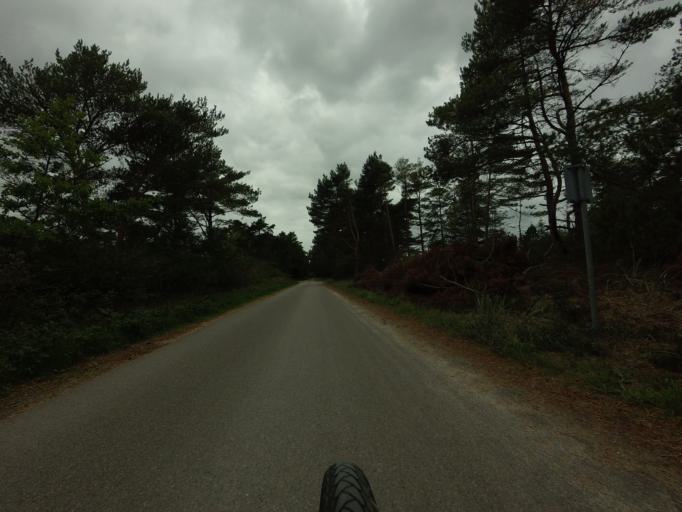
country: DK
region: North Denmark
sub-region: Hjorring Kommune
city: Sindal
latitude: 57.6109
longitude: 10.2837
